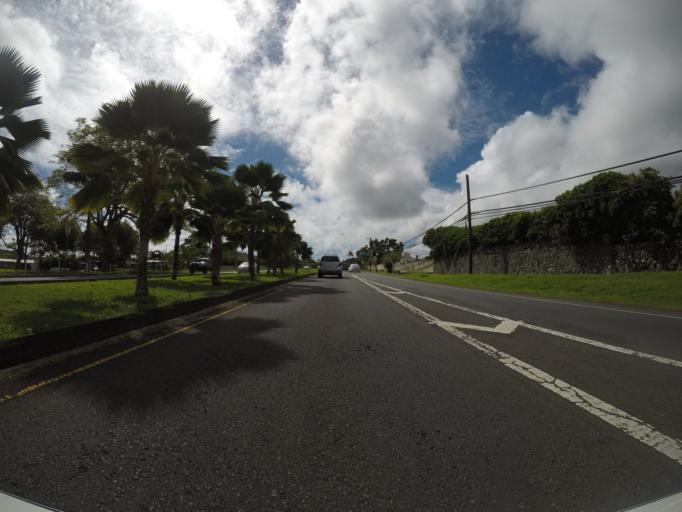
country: US
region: Hawaii
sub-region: Honolulu County
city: Maunawili
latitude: 21.3804
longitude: -157.7555
